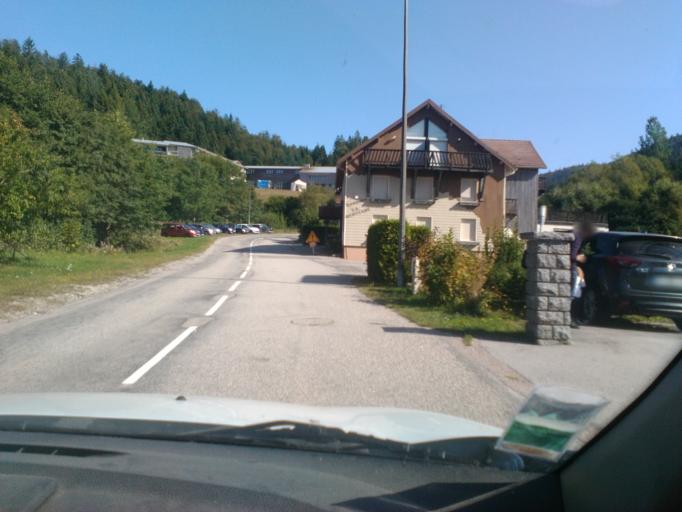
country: FR
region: Lorraine
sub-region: Departement des Vosges
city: Xonrupt-Longemer
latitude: 48.0347
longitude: 6.9238
